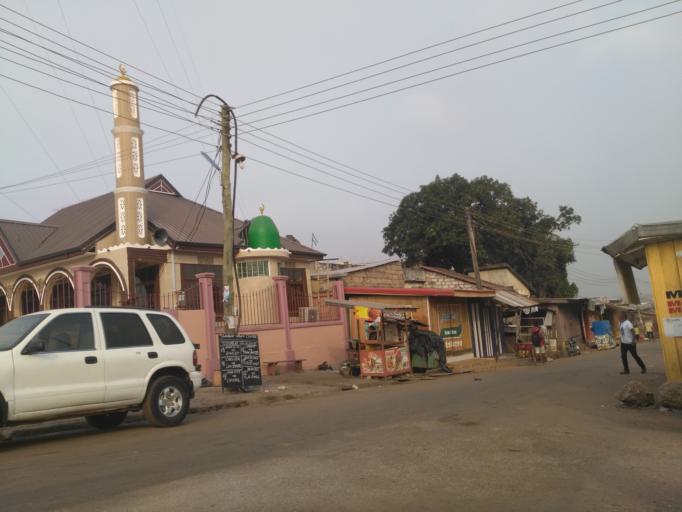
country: GH
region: Ashanti
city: Kumasi
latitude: 6.6942
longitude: -1.6137
